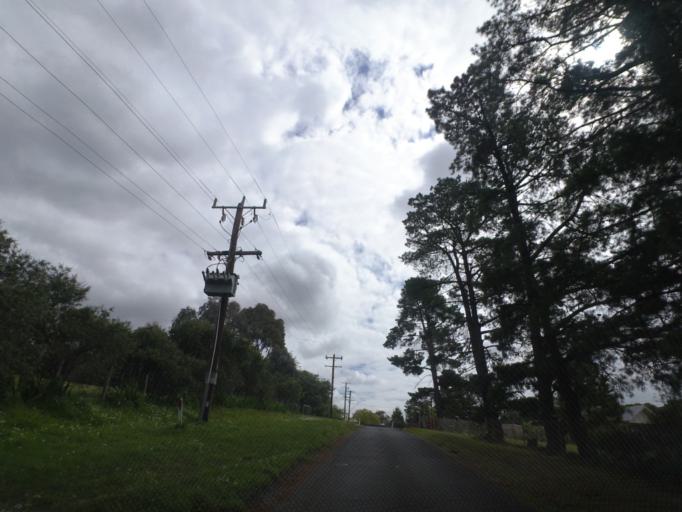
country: AU
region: Victoria
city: Plenty
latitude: -37.6642
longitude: 145.1090
